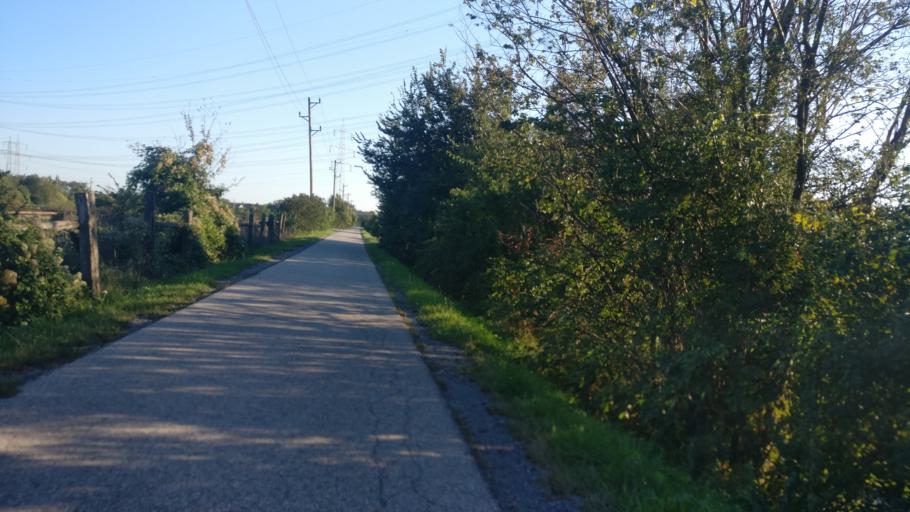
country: AT
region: Lower Austria
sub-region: Politischer Bezirk Wien-Umgebung
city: Lanzendorf
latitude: 48.0998
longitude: 16.4420
